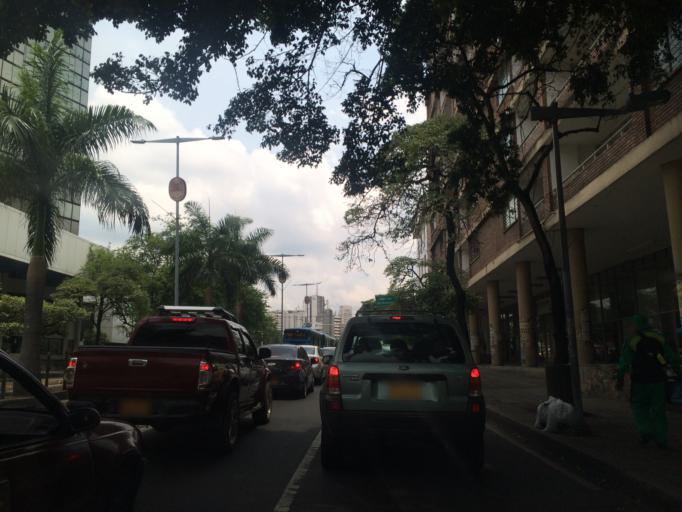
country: CO
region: Valle del Cauca
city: Cali
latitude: 3.4591
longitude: -76.5287
